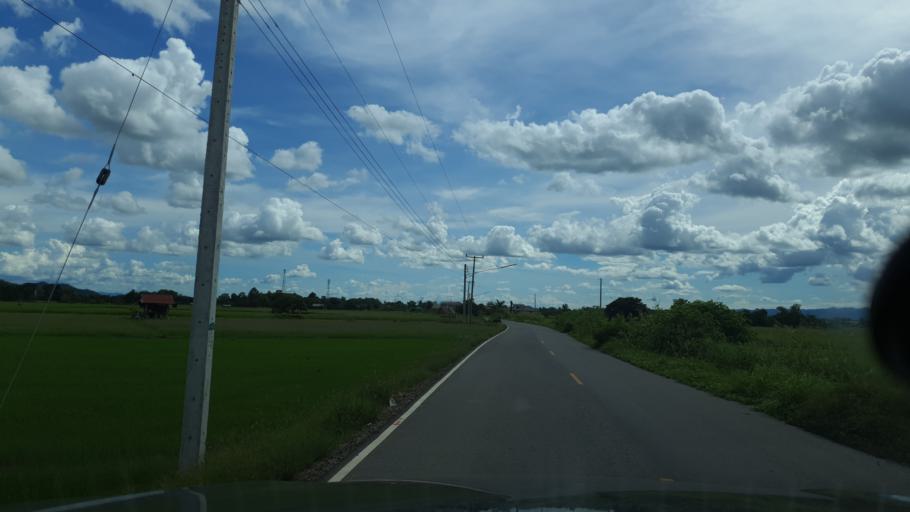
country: TH
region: Sukhothai
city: Thung Saliam
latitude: 17.3392
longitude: 99.6344
